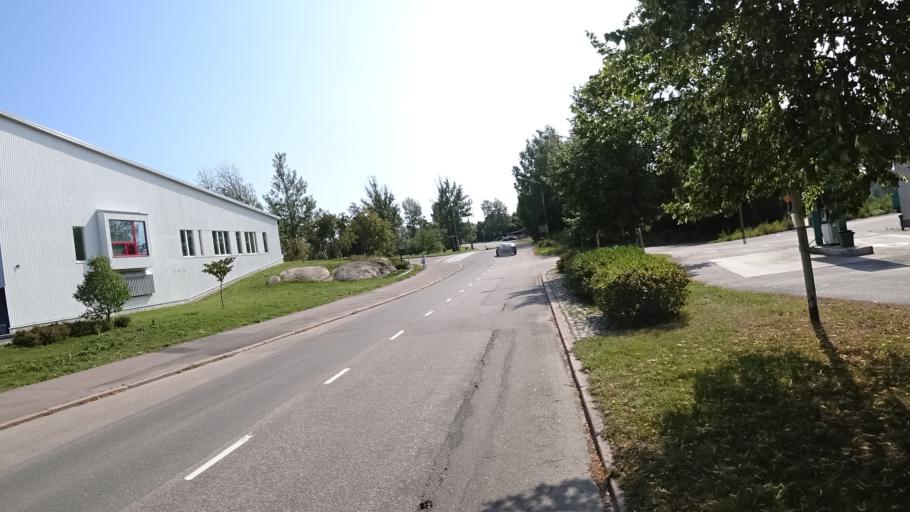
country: FI
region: Kymenlaakso
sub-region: Kotka-Hamina
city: Kotka
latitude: 60.4556
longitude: 26.9368
